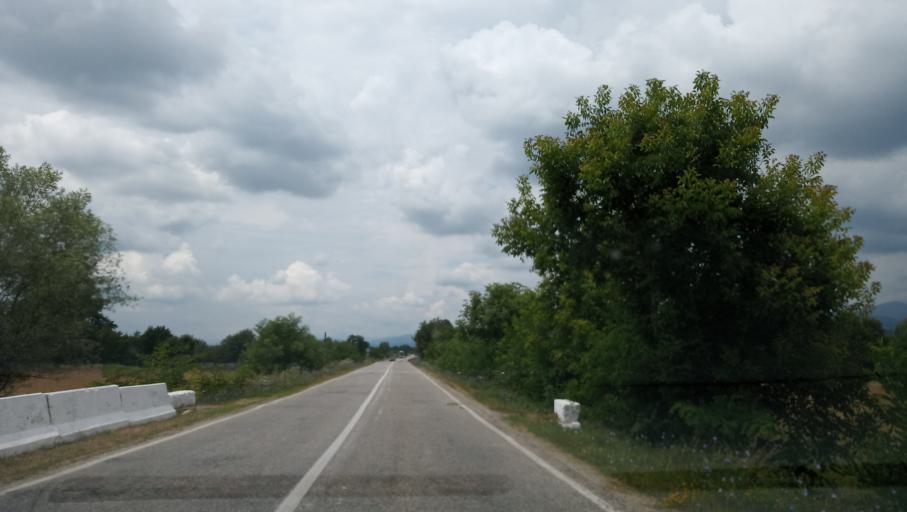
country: RO
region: Gorj
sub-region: Comuna Runcu
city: Valea Mare
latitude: 45.0871
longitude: 23.0947
